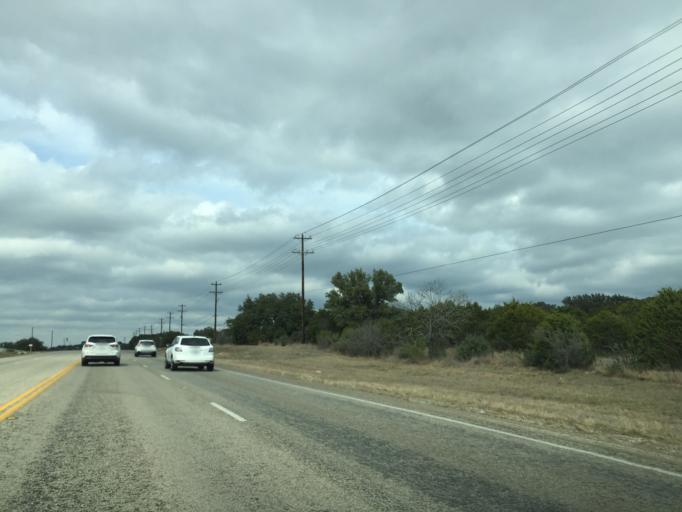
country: US
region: Texas
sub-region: Travis County
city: Briarcliff
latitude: 30.3975
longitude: -98.0897
